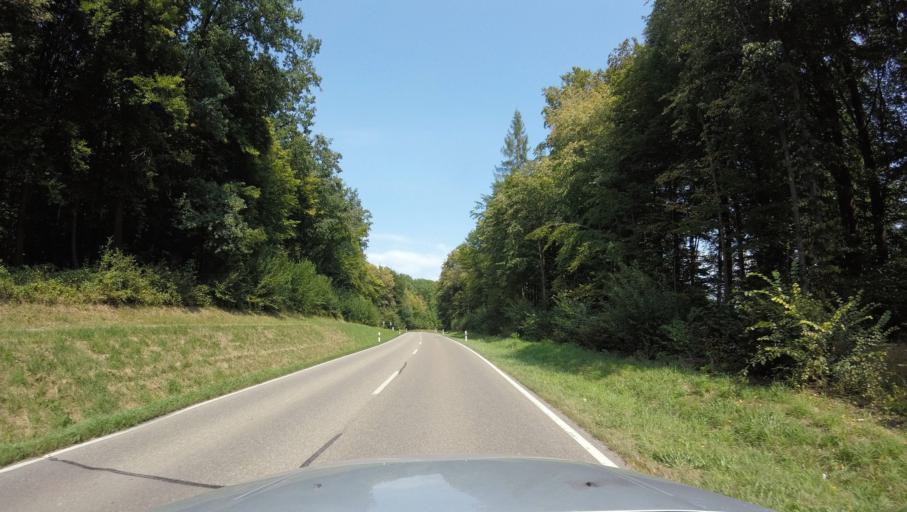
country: DE
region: Baden-Wuerttemberg
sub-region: Regierungsbezirk Stuttgart
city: Backnang
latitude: 48.9546
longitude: 9.4590
